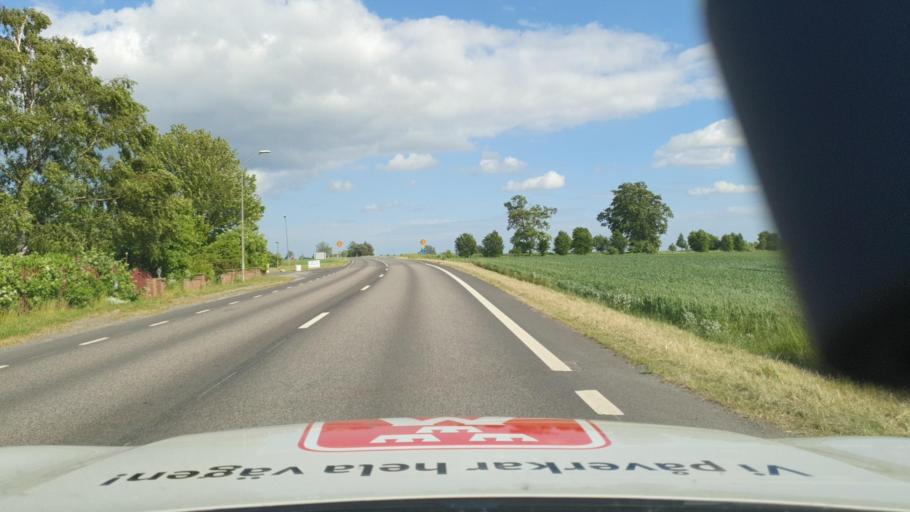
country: SE
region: Skane
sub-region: Simrishamns Kommun
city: Kivik
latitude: 55.5424
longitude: 14.1992
